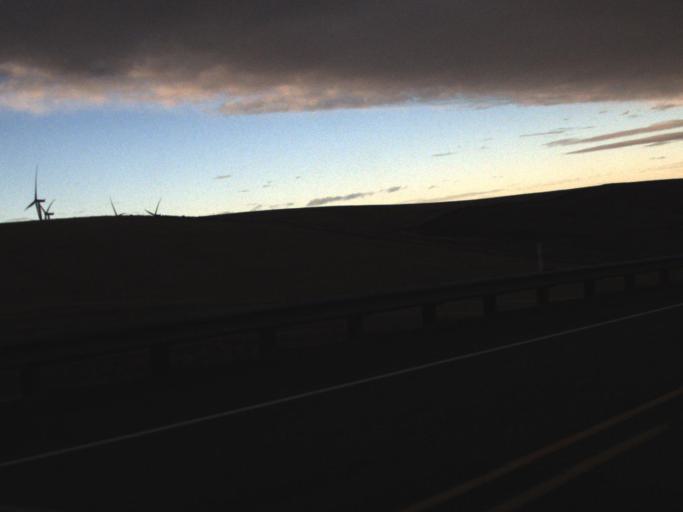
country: US
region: Washington
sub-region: Garfield County
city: Pomeroy
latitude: 46.5408
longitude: -117.7760
